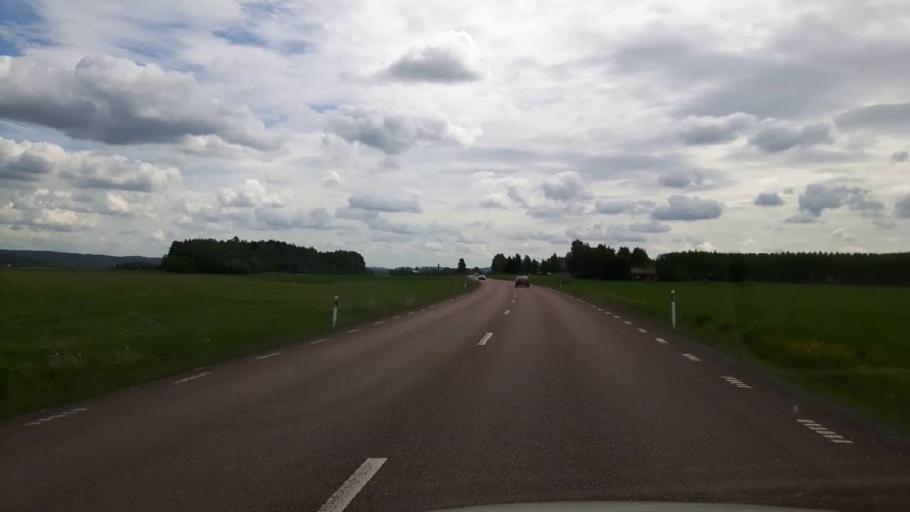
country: SE
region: Dalarna
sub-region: Hedemora Kommun
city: Hedemora
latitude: 60.3139
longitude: 15.9643
